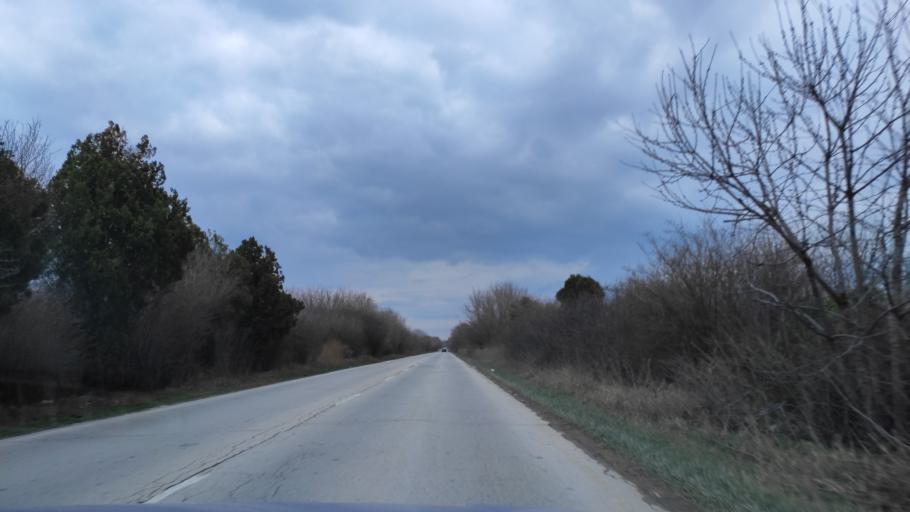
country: BG
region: Varna
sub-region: Obshtina Aksakovo
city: Aksakovo
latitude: 43.2289
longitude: 27.8337
